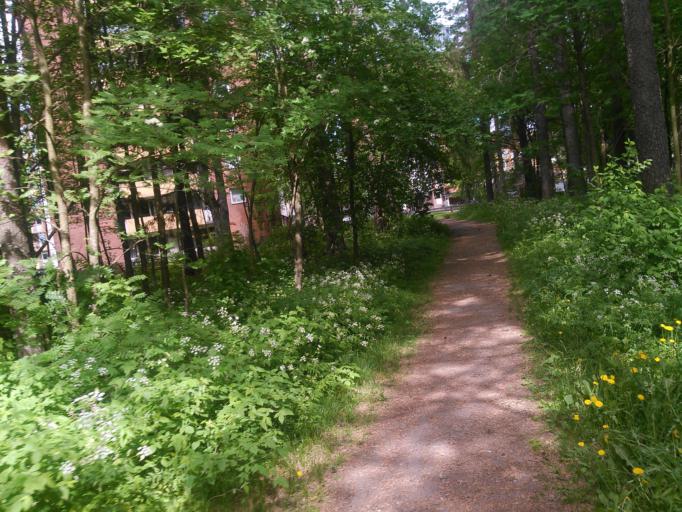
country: SE
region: Vaesterbotten
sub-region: Umea Kommun
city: Umea
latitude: 63.8126
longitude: 20.3004
